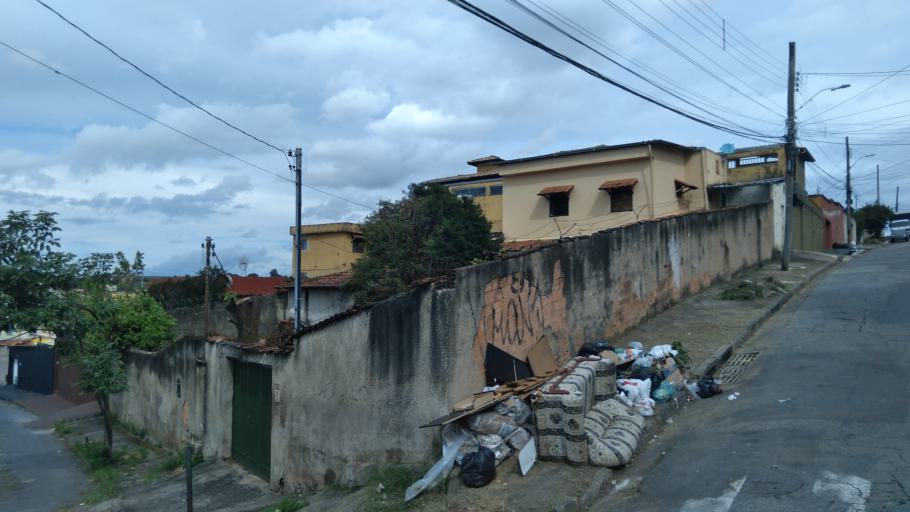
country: BR
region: Minas Gerais
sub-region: Contagem
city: Contagem
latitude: -19.9102
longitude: -44.0069
